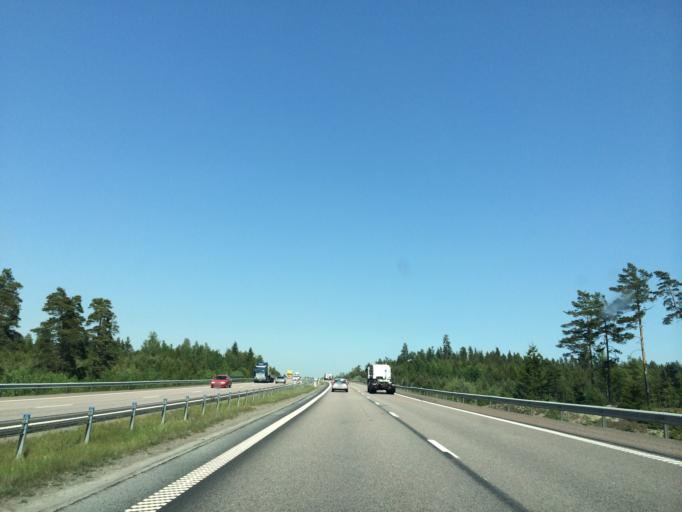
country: SE
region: OEstergoetland
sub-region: Norrkopings Kommun
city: Krokek
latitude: 58.7095
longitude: 16.3608
